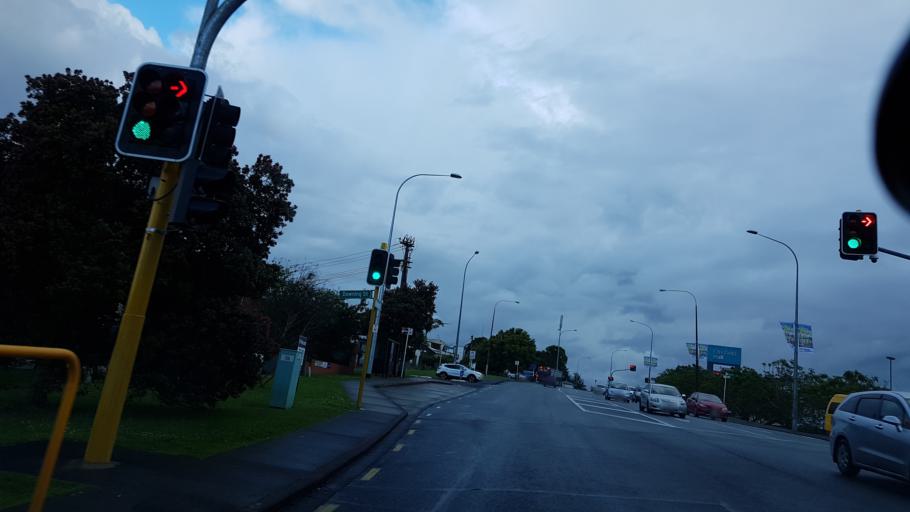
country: NZ
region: Auckland
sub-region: Auckland
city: North Shore
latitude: -36.7838
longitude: 174.7215
